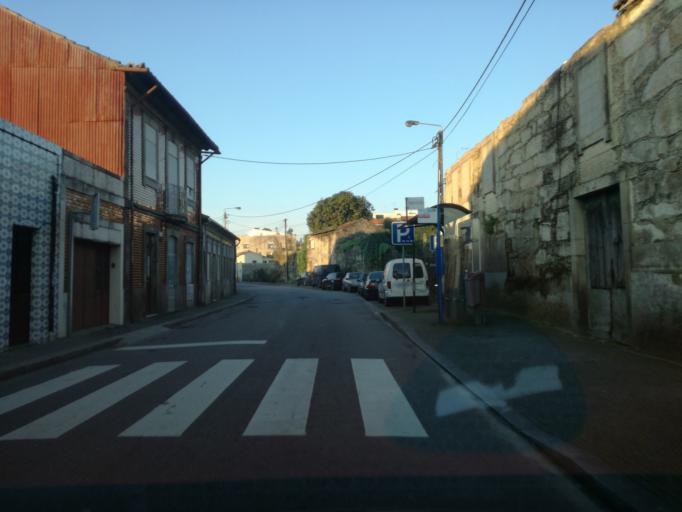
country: PT
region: Porto
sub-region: Maia
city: Milheiros
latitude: 41.2191
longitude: -8.5916
